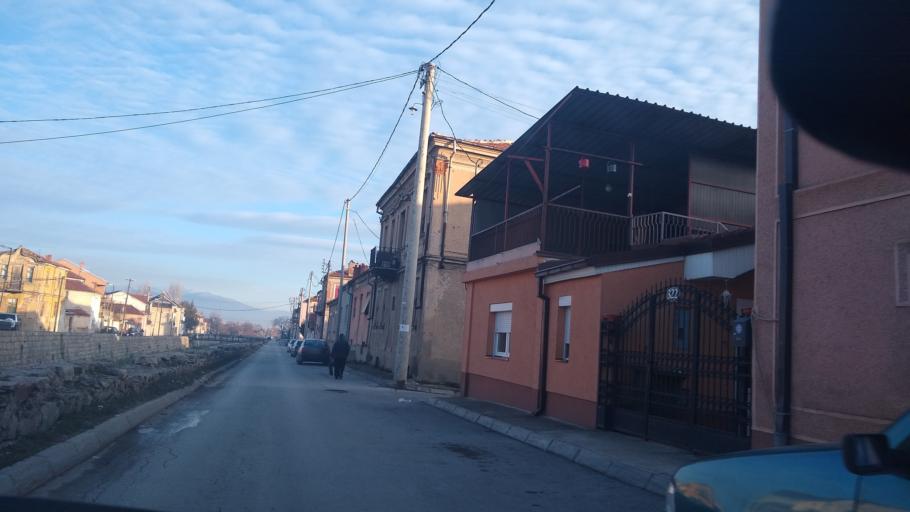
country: MK
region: Bitola
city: Bitola
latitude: 41.0310
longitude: 21.3421
